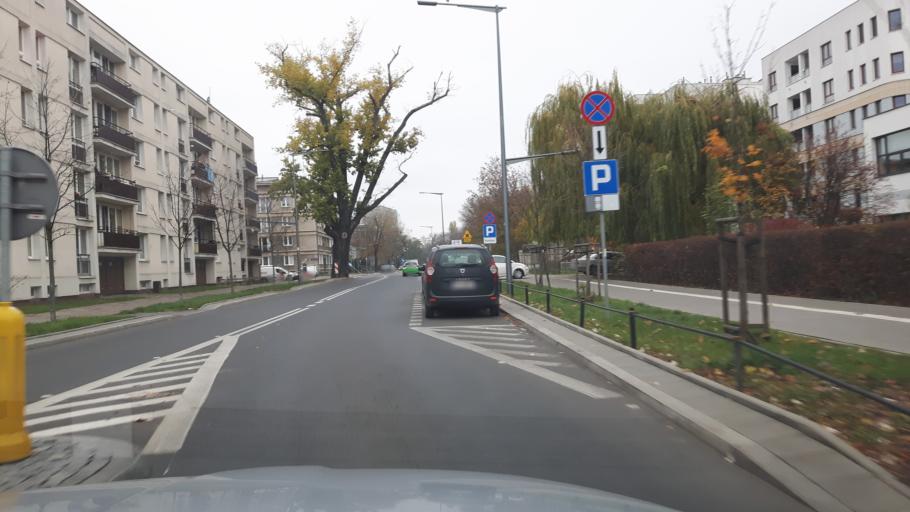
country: PL
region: Masovian Voivodeship
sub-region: Warszawa
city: Praga Polnoc
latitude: 52.2624
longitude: 21.0352
